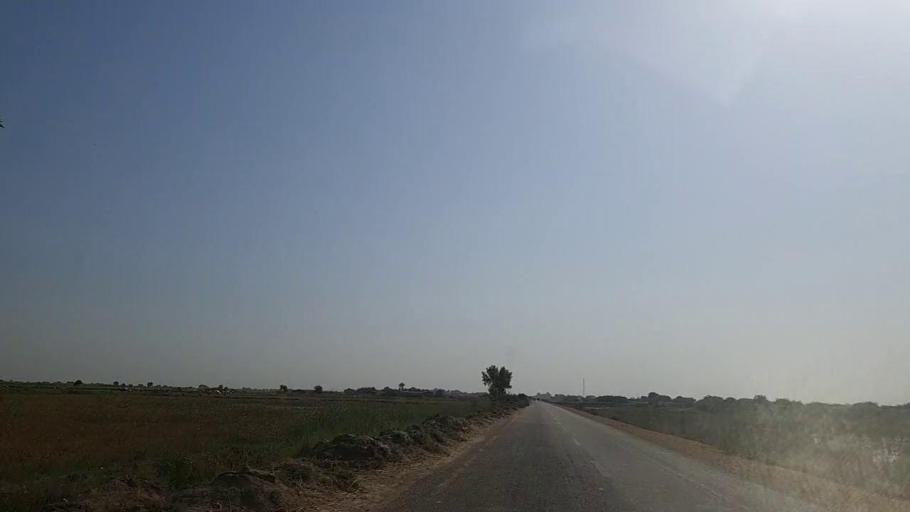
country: PK
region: Sindh
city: Jati
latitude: 24.5316
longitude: 68.2781
